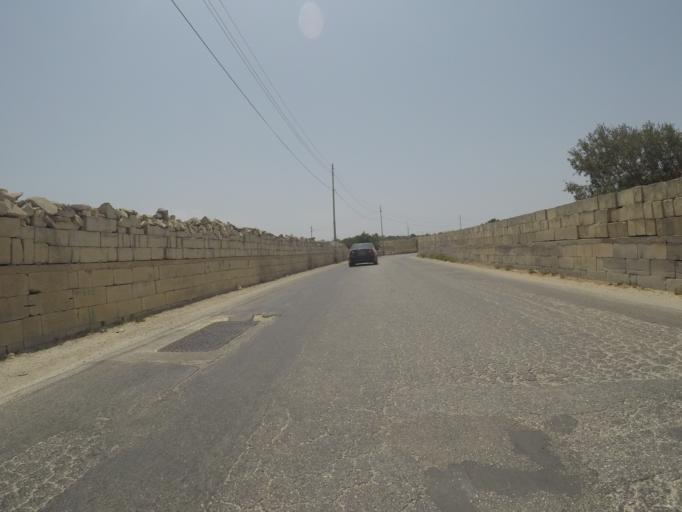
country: MT
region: Is-Siggiewi
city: Siggiewi
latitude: 35.8475
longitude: 14.4342
